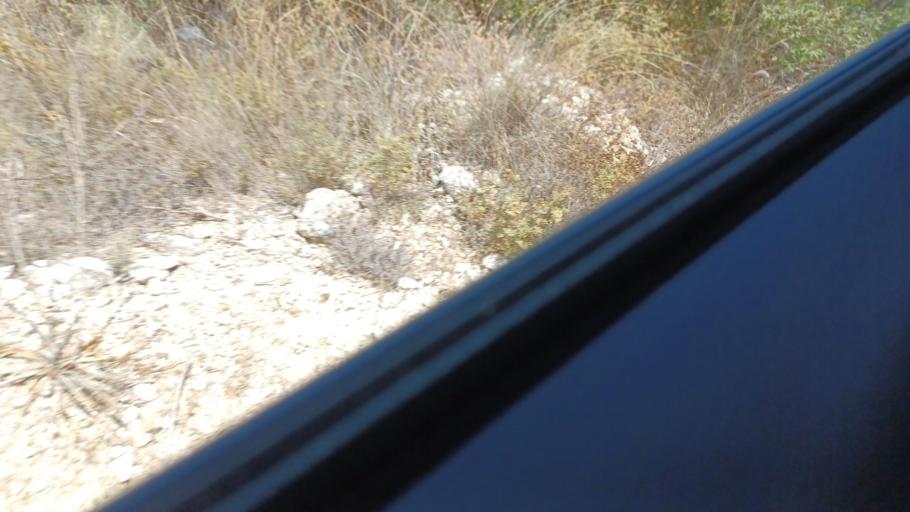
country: CY
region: Pafos
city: Tala
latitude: 34.8704
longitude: 32.4312
